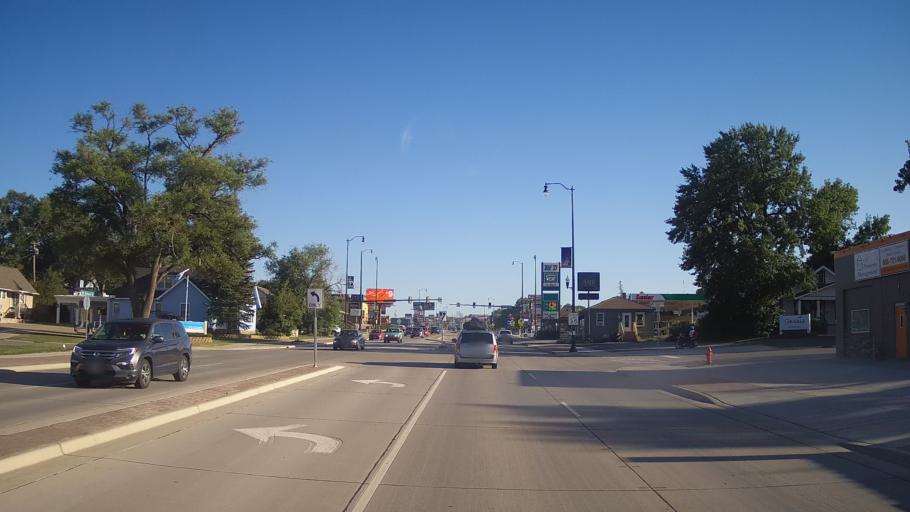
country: US
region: South Dakota
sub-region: Pennington County
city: Rapid City
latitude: 44.0722
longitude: -103.2325
